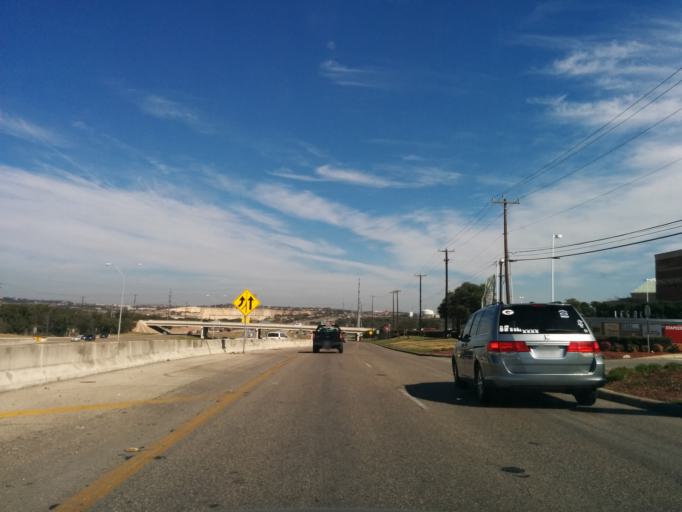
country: US
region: Texas
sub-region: Bexar County
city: Hollywood Park
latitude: 29.6112
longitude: -98.4674
